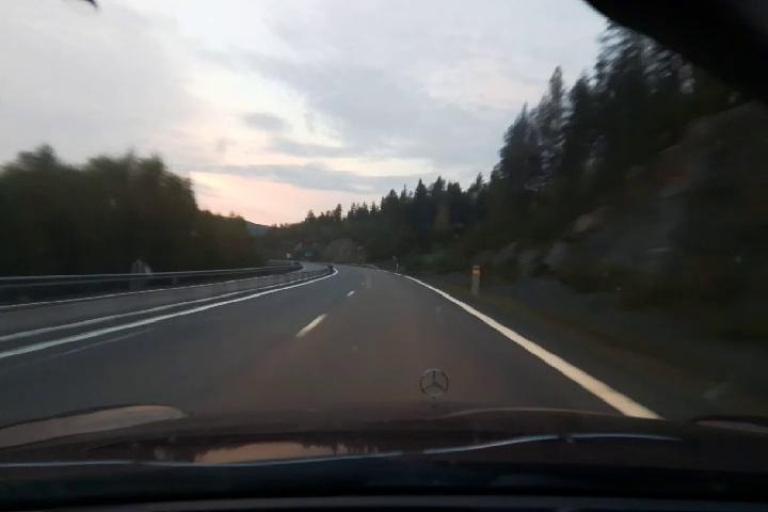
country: SE
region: Vaesternorrland
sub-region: Kramfors Kommun
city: Nordingra
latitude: 62.9449
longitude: 18.0936
